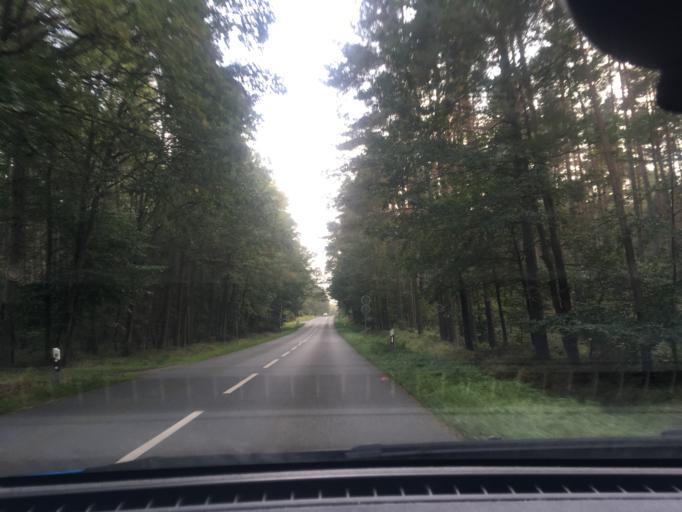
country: DE
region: Lower Saxony
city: Barendorf
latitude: 53.2539
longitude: 10.5271
